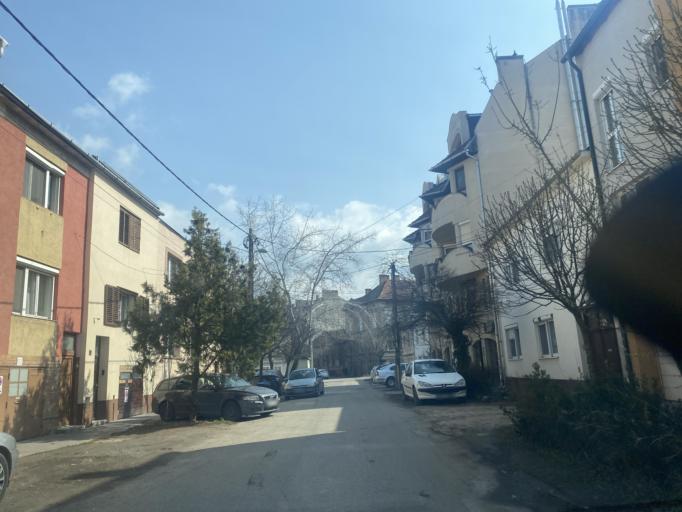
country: HU
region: Csongrad
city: Szeged
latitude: 46.2627
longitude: 20.1519
